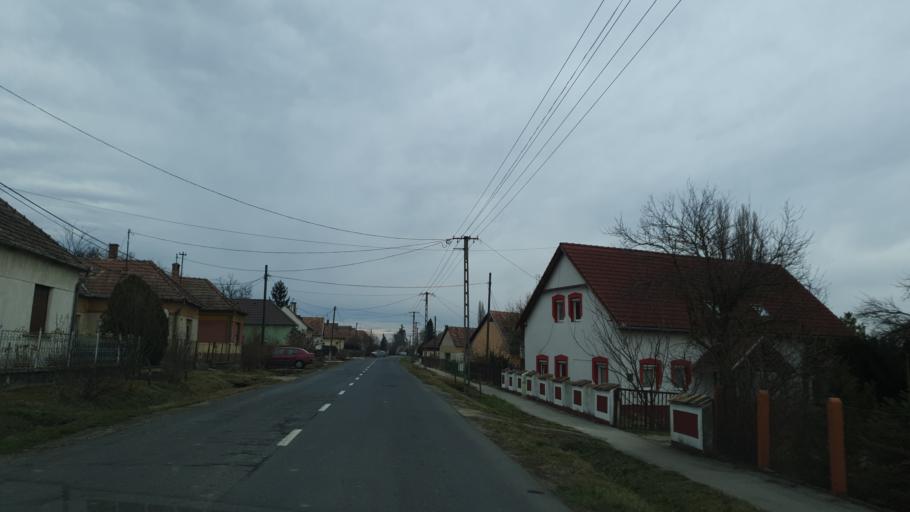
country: HU
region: Zala
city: Sarmellek
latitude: 46.7051
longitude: 17.1087
